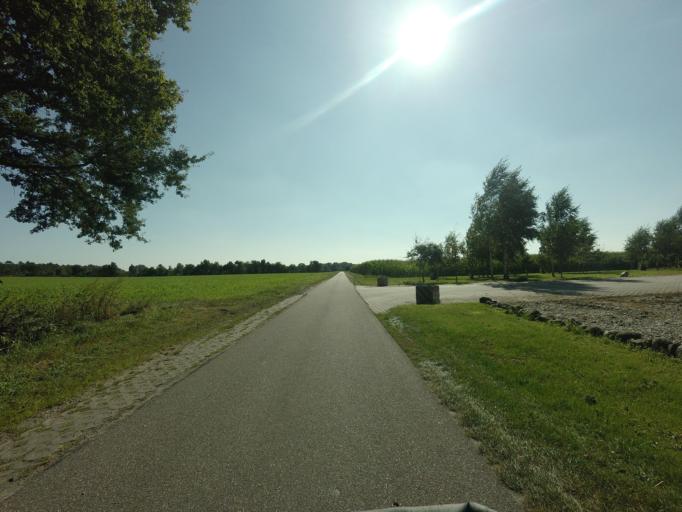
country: DE
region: Lower Saxony
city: Wielen
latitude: 52.5263
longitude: 6.7090
